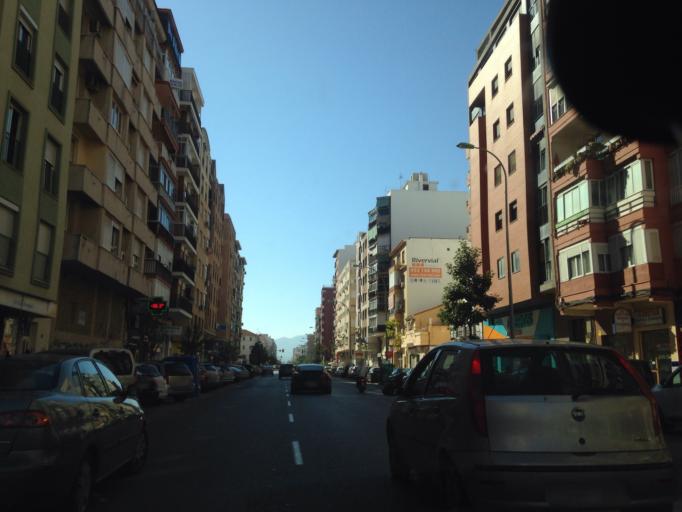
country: ES
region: Andalusia
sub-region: Provincia de Malaga
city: Malaga
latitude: 36.7035
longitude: -4.4410
